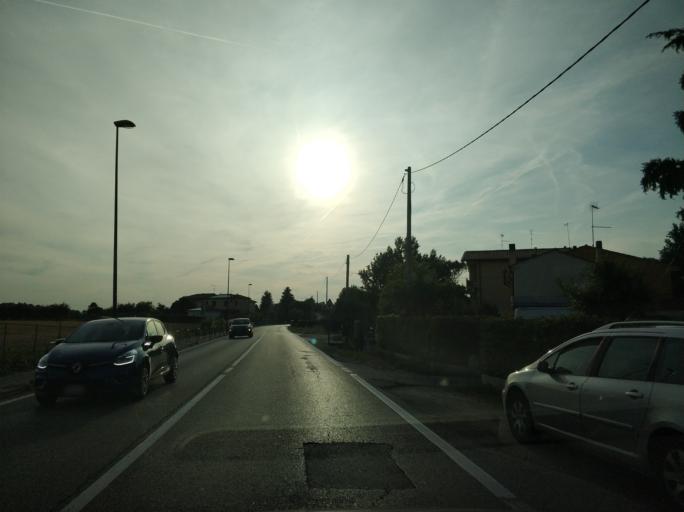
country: IT
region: Veneto
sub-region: Provincia di Padova
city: Este
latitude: 45.2105
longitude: 11.6820
